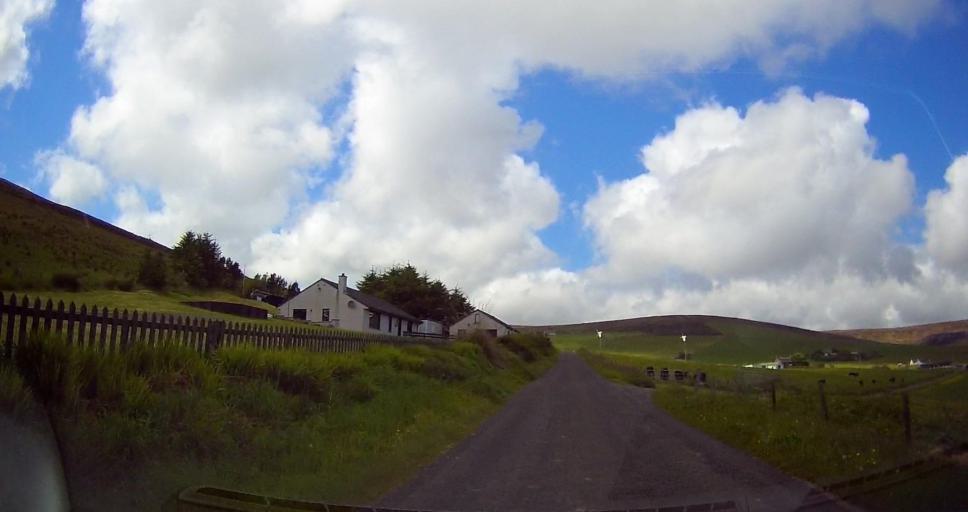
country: GB
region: Scotland
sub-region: Orkney Islands
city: Orkney
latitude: 59.0484
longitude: -3.1001
